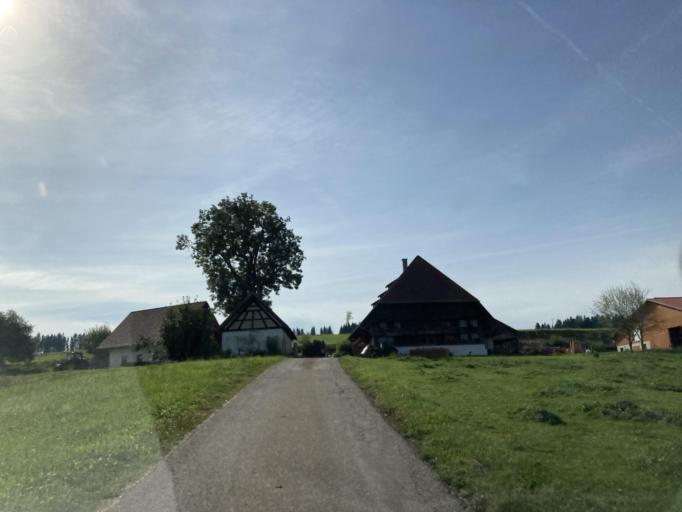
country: DE
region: Baden-Wuerttemberg
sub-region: Freiburg Region
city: Schonwald im Schwarzwald
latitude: 48.0878
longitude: 8.2339
